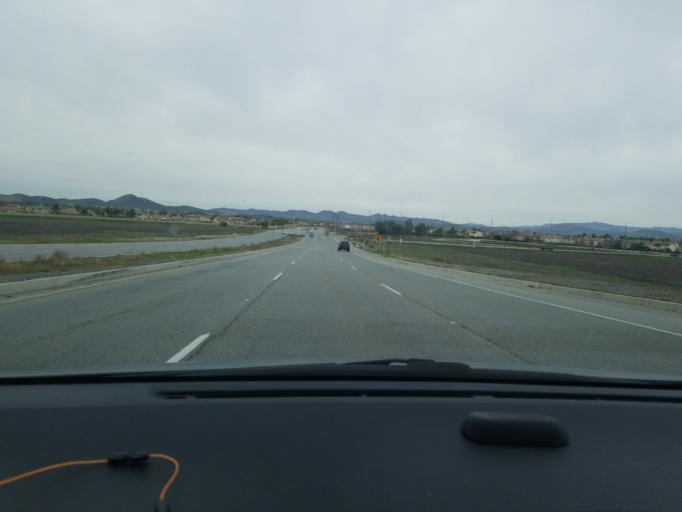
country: US
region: California
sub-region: Riverside County
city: Menifee
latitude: 33.6923
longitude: -117.1409
